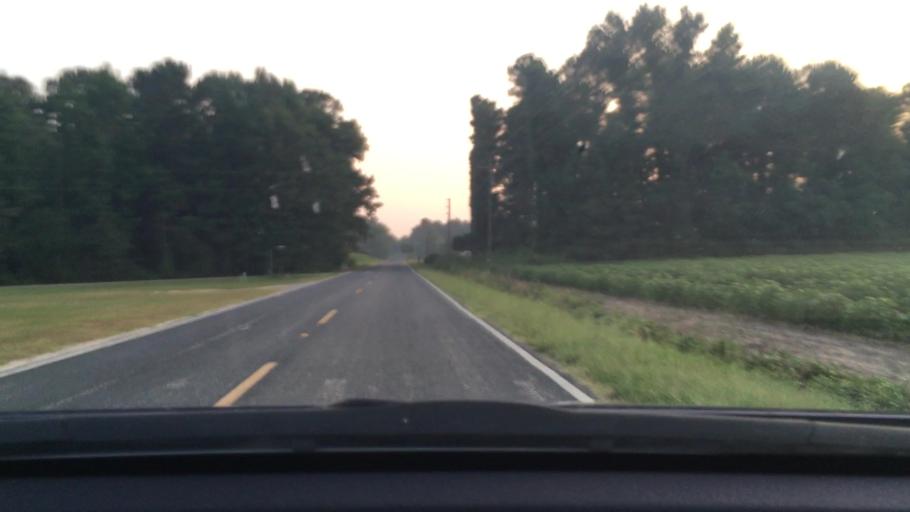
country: US
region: South Carolina
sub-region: Lee County
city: Bishopville
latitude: 34.1867
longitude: -80.1423
